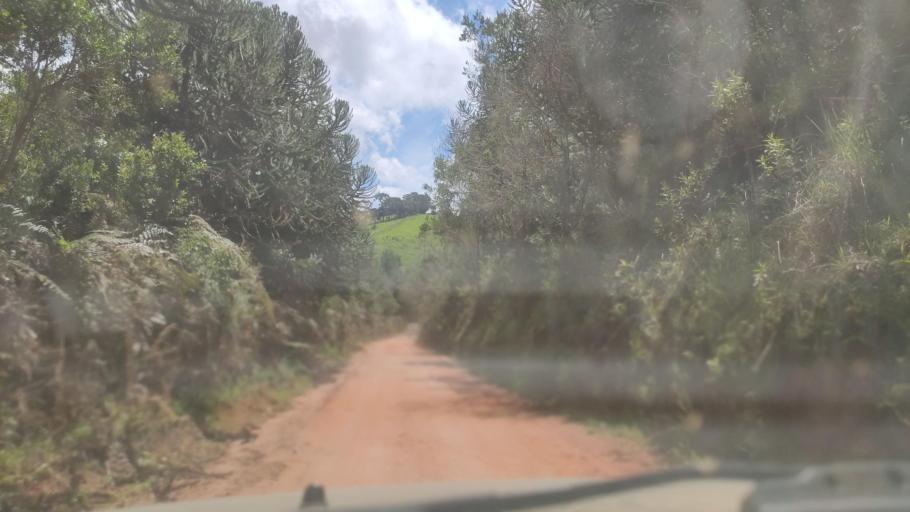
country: BR
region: Minas Gerais
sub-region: Cambui
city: Cambui
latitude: -22.6821
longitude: -45.9745
